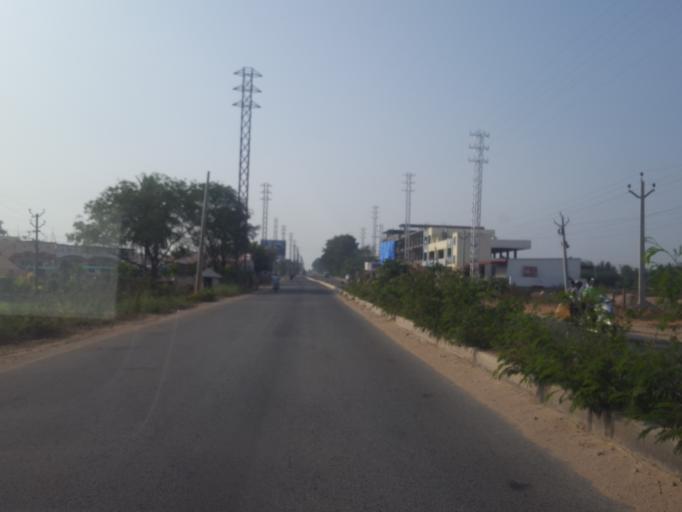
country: IN
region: Telangana
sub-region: Medak
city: Serilingampalle
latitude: 17.4039
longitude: 78.2874
